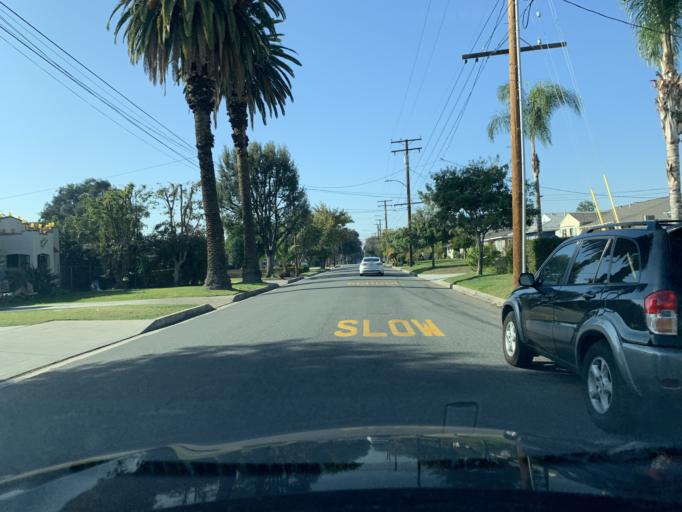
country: US
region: California
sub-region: Los Angeles County
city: Covina
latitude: 34.0826
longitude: -117.8820
